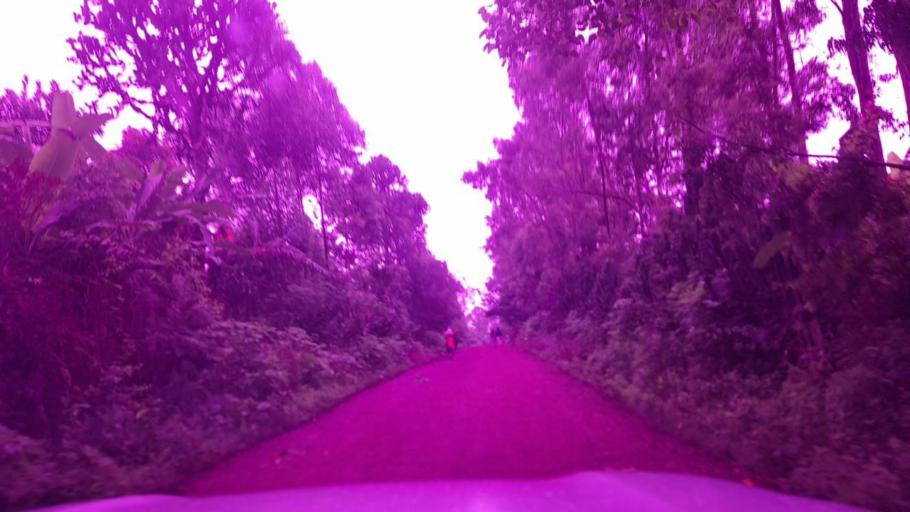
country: ET
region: Southern Nations, Nationalities, and People's Region
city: Bonga
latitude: 7.5832
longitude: 36.0190
